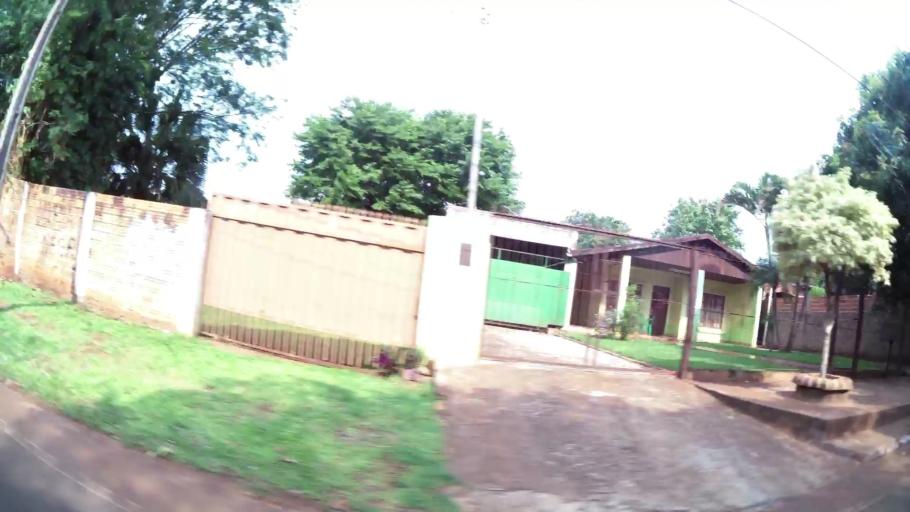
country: PY
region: Alto Parana
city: Ciudad del Este
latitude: -25.4957
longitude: -54.6500
